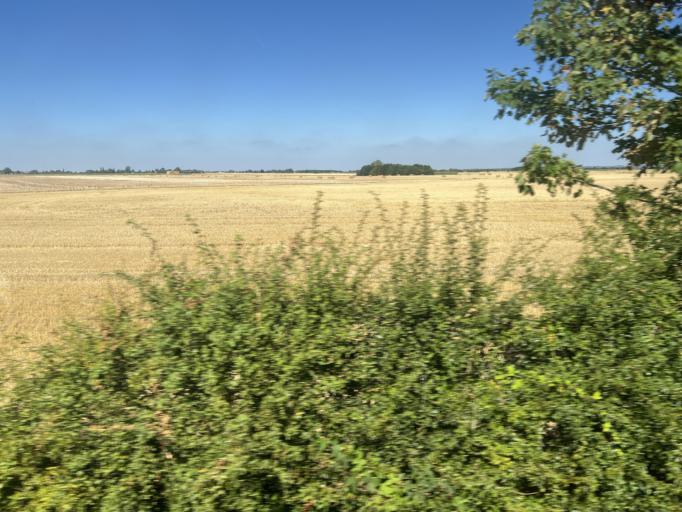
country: GB
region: England
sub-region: Lincolnshire
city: Boston
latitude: 53.0485
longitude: 0.0437
